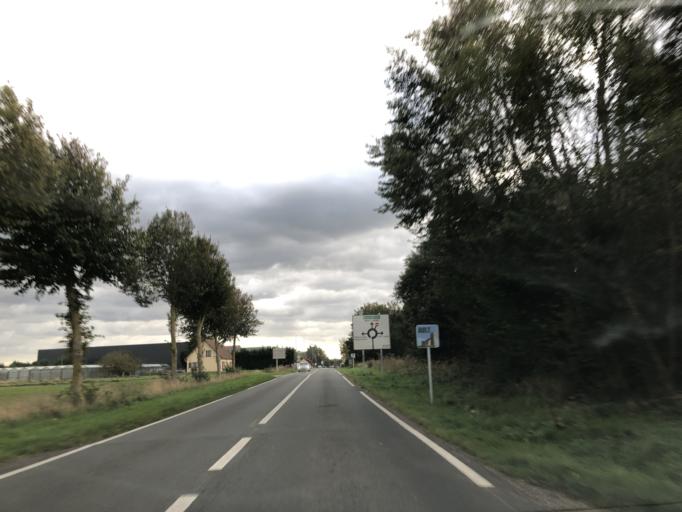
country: FR
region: Picardie
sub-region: Departement de la Somme
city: Ault
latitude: 50.0973
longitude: 1.4659
